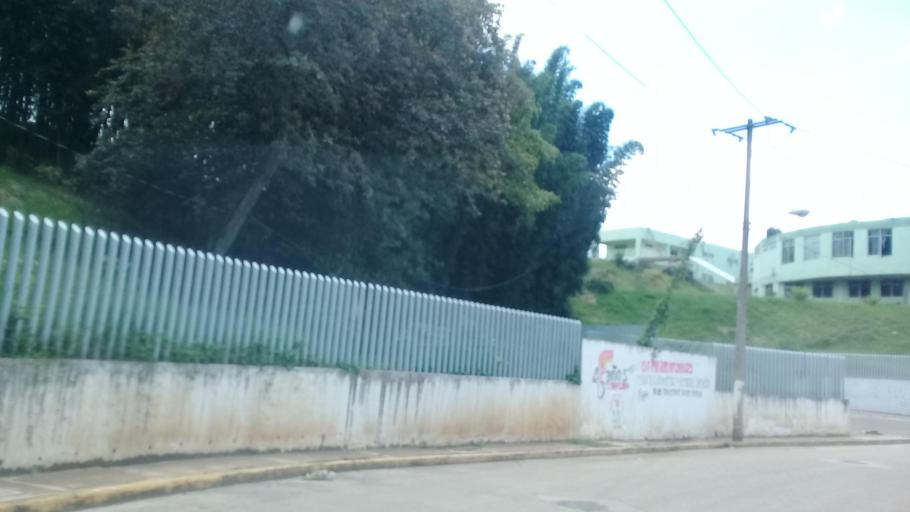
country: MX
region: Veracruz
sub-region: Xalapa
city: Fraccionamiento las Fuentes
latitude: 19.4992
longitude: -96.8835
